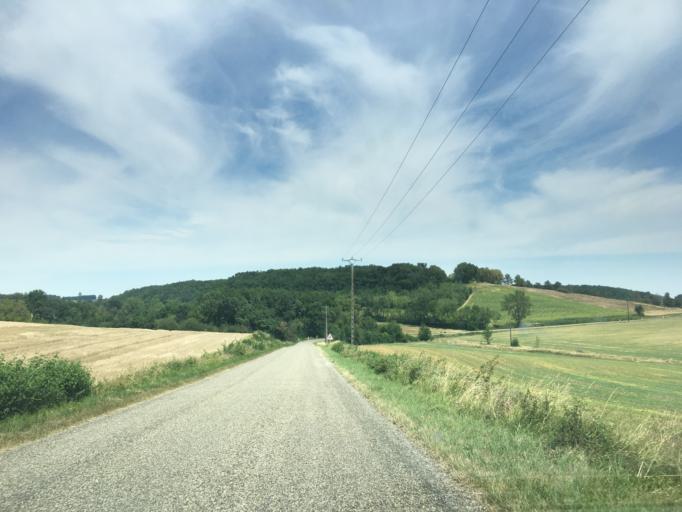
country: FR
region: Midi-Pyrenees
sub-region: Departement du Gers
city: Jegun
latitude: 43.8098
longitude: 0.5104
